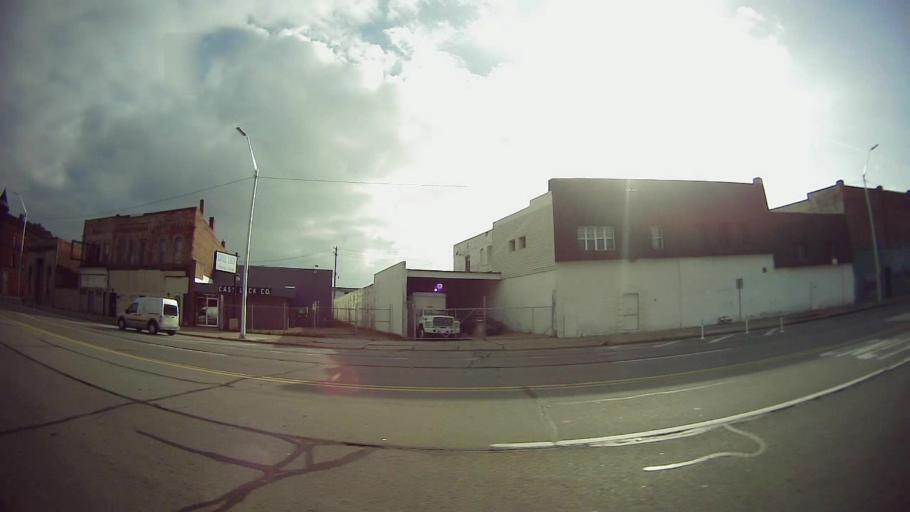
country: US
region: Michigan
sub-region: Wayne County
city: Detroit
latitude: 42.3315
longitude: -83.0913
